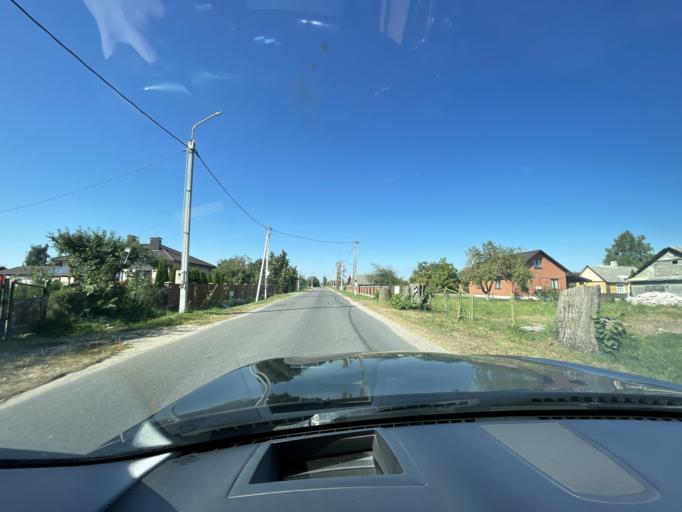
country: BY
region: Grodnenskaya
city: Hrodna
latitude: 53.7266
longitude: 23.9876
